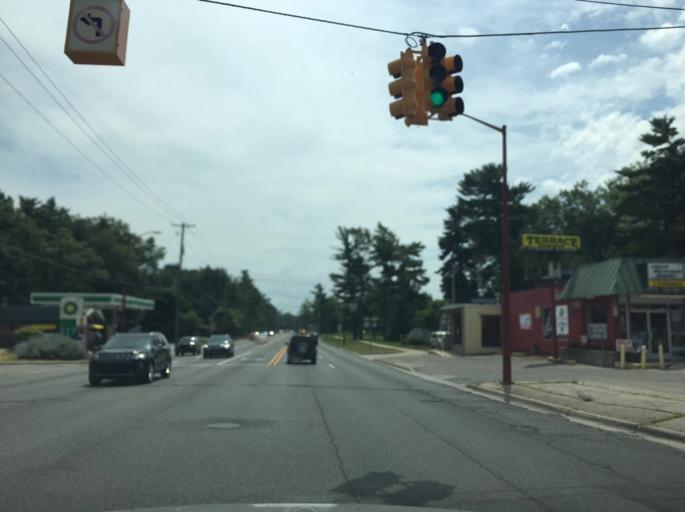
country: US
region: Michigan
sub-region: Grand Traverse County
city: Traverse City
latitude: 44.7587
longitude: -85.5791
